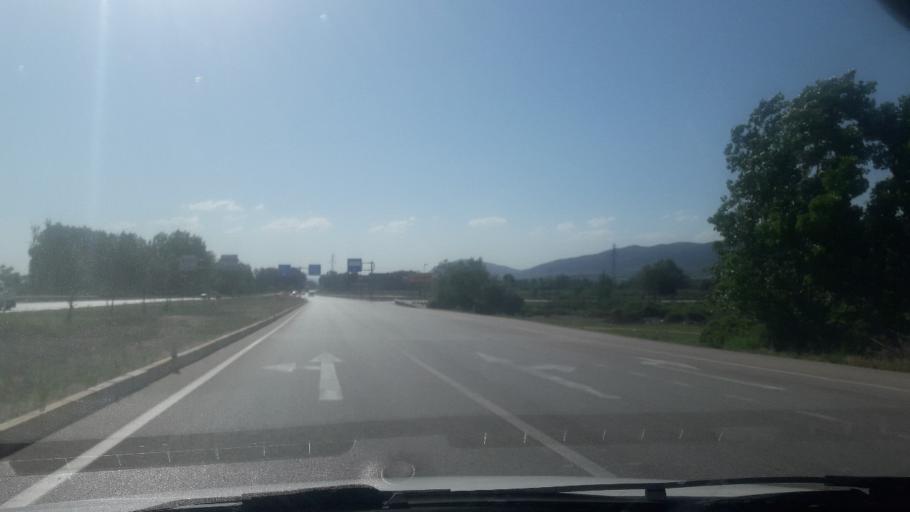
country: TR
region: Tokat
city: Yesilyurt
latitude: 40.2986
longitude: 36.3623
